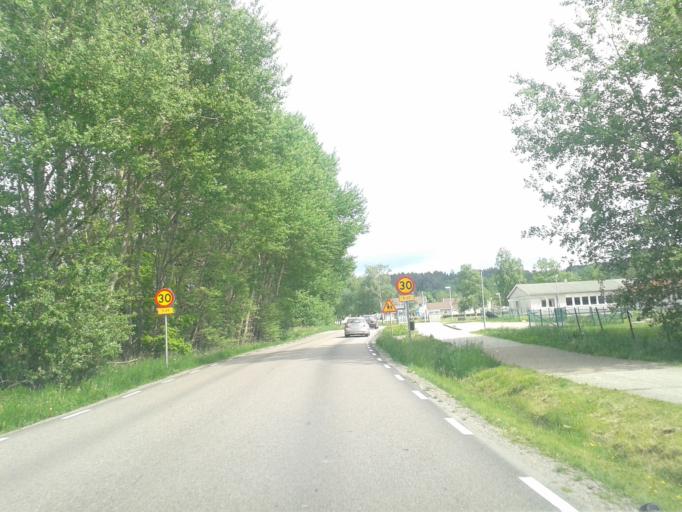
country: SE
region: Vaestra Goetaland
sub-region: Kungalvs Kommun
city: Kungalv
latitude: 57.9054
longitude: 11.9254
